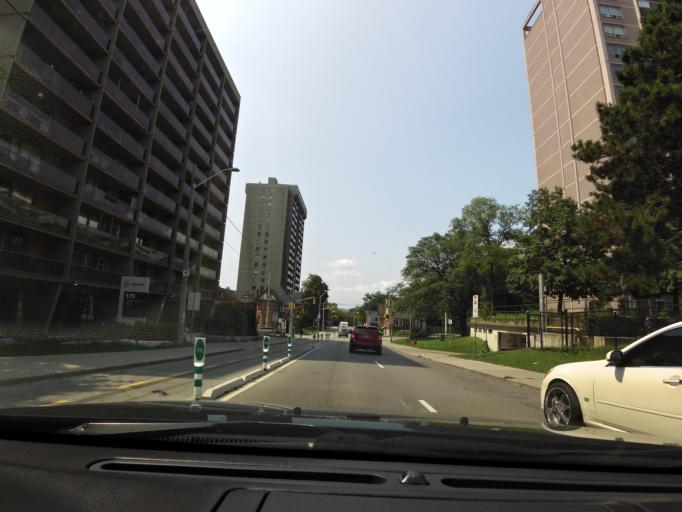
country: CA
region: Ontario
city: Hamilton
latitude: 43.2554
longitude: -79.8780
